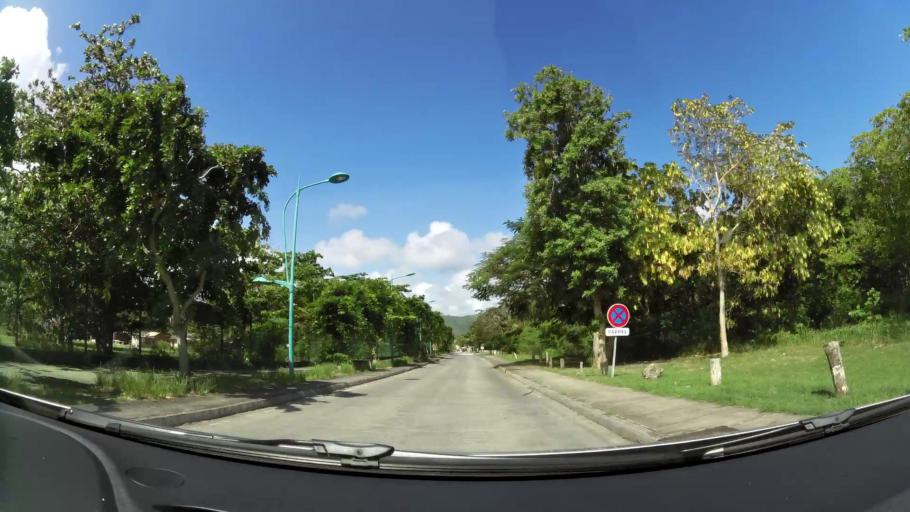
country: MQ
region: Martinique
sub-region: Martinique
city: Le Marin
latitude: 14.4417
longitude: -60.8788
